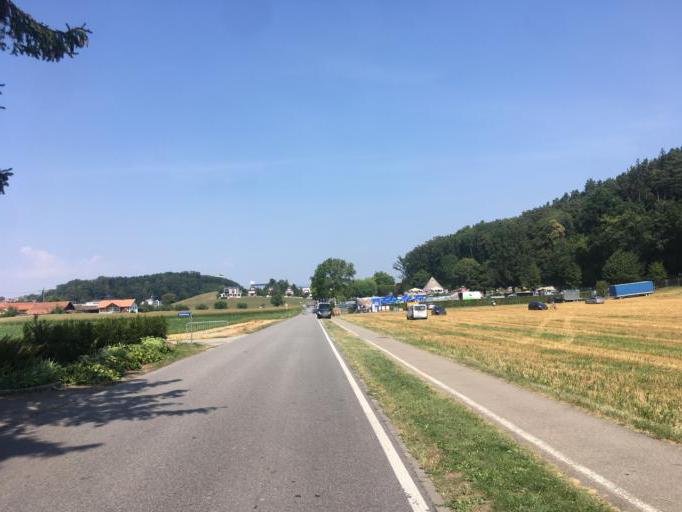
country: CH
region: Bern
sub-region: Bern-Mittelland District
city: Muri
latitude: 46.9440
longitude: 7.4944
